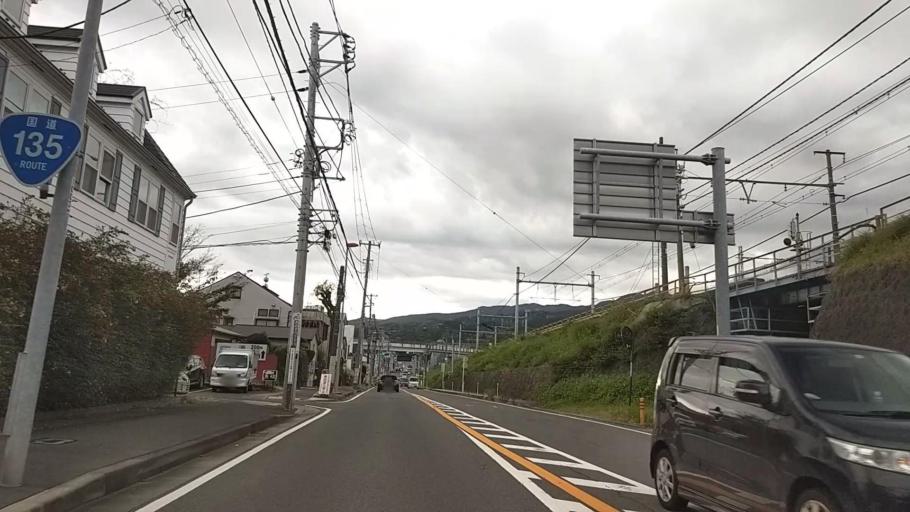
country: JP
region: Kanagawa
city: Odawara
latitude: 35.2458
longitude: 139.1491
